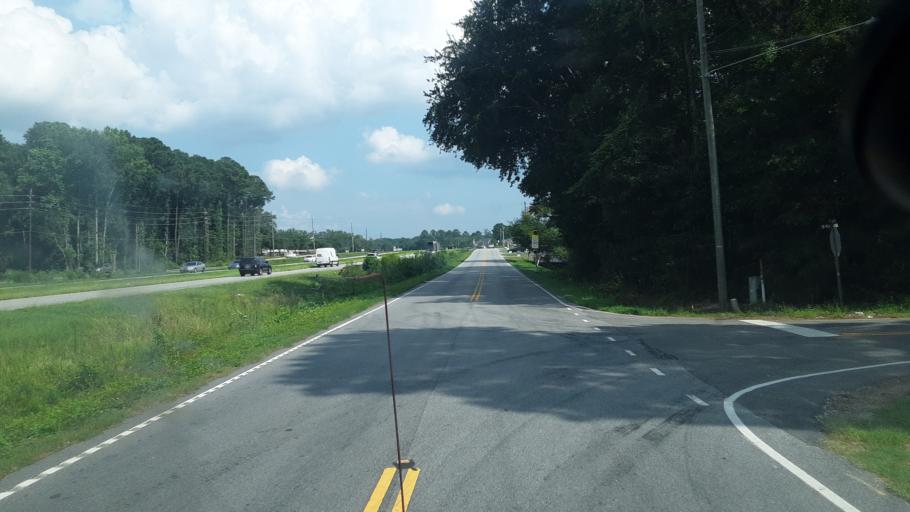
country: US
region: South Carolina
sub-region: Sumter County
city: Sumter
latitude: 33.9500
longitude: -80.3620
